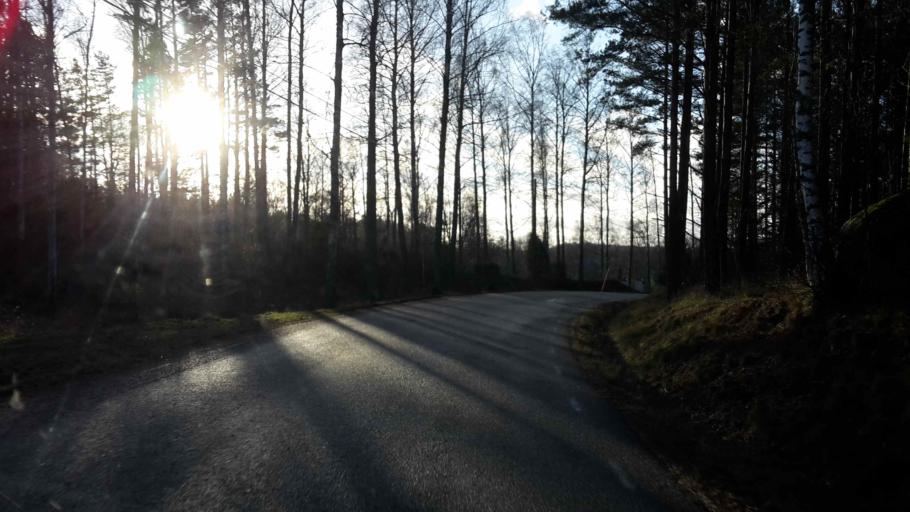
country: SE
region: OEstergoetland
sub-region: Atvidabergs Kommun
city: Atvidaberg
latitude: 58.2643
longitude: 16.1411
